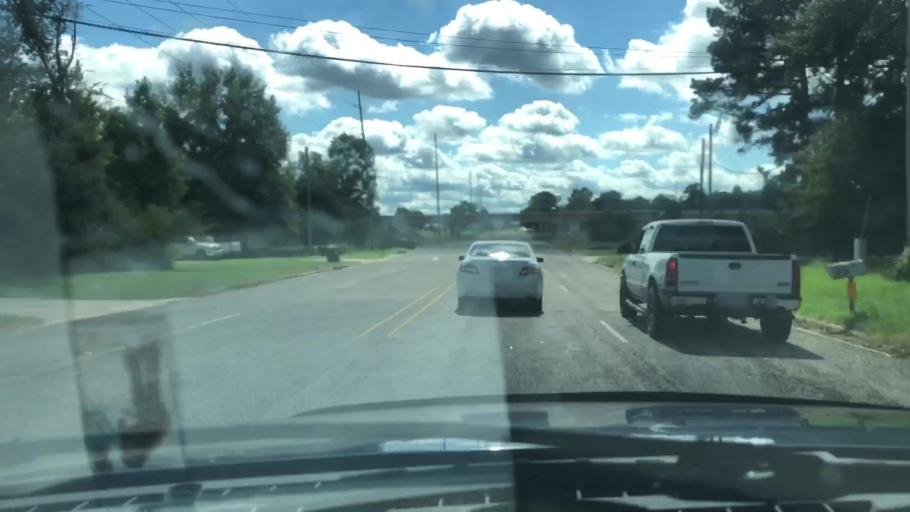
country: US
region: Texas
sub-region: Bowie County
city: Wake Village
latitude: 33.3890
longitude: -94.0922
